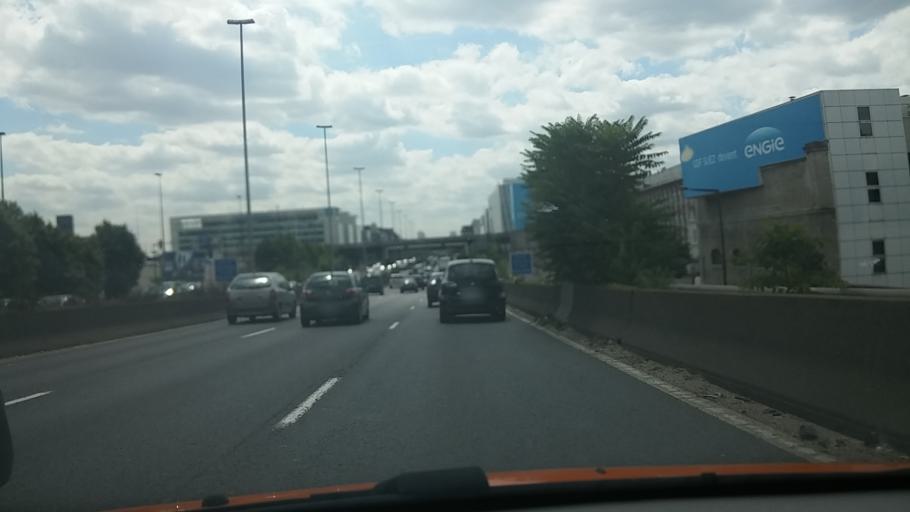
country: FR
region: Ile-de-France
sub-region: Departement de Seine-Saint-Denis
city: Saint-Denis
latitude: 48.9255
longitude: 2.3568
